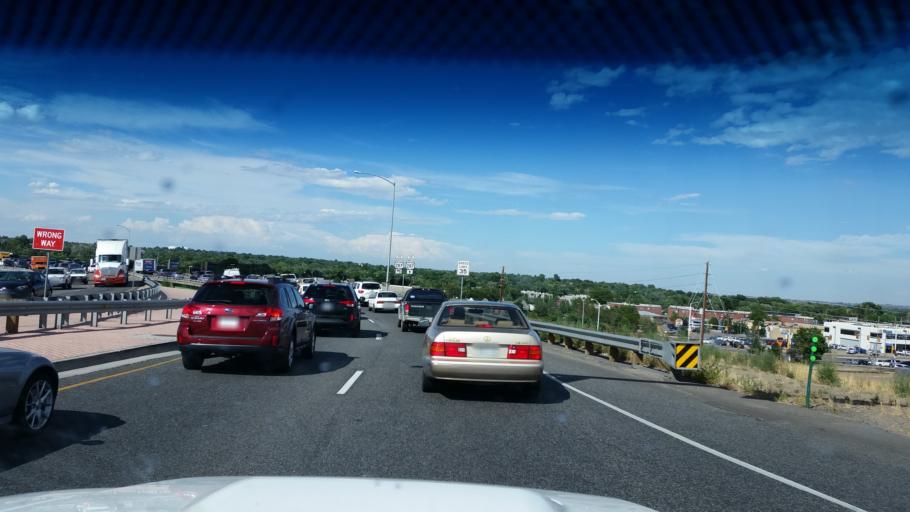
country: US
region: Colorado
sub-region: Broomfield County
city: Broomfield
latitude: 39.9176
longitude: -105.0915
